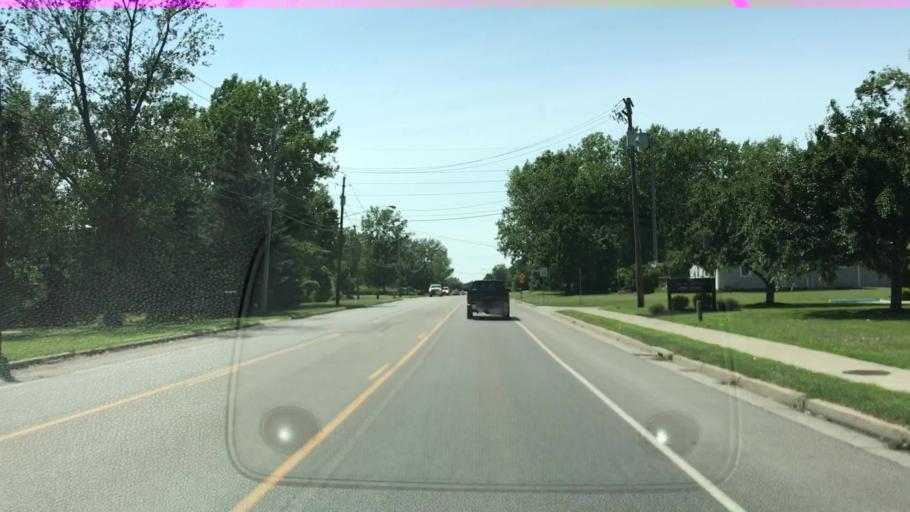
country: US
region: New York
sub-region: Erie County
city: Cheektowaga
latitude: 42.8816
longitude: -78.7342
